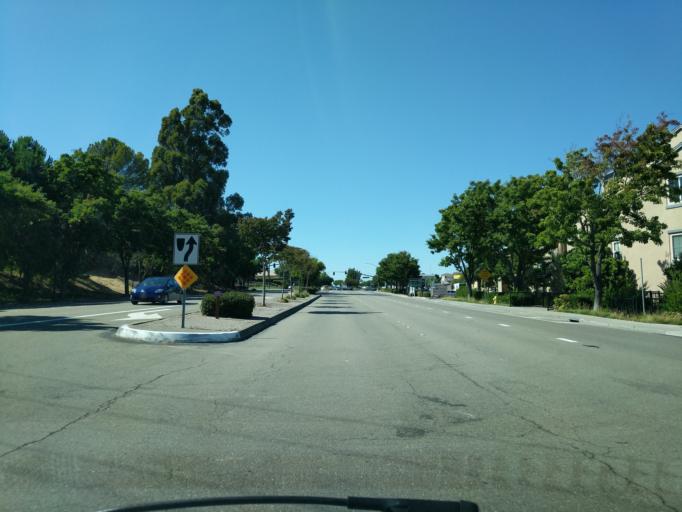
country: US
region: California
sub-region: Alameda County
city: Dublin
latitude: 37.7216
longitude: -121.9419
